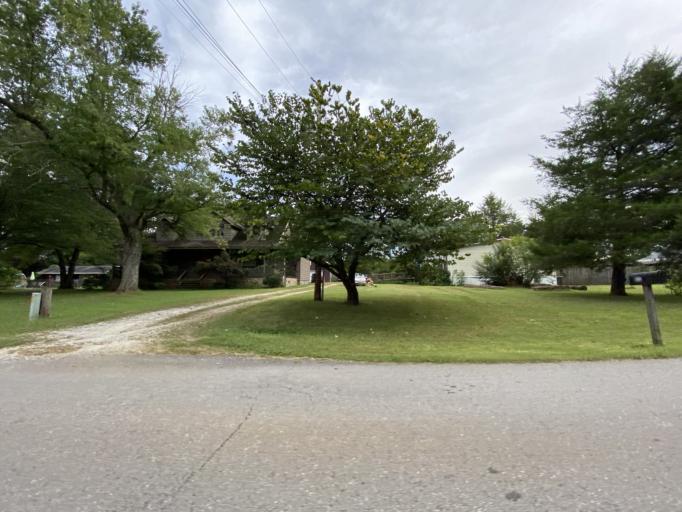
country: US
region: Alabama
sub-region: Madison County
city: Hazel Green
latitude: 34.9022
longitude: -86.6640
